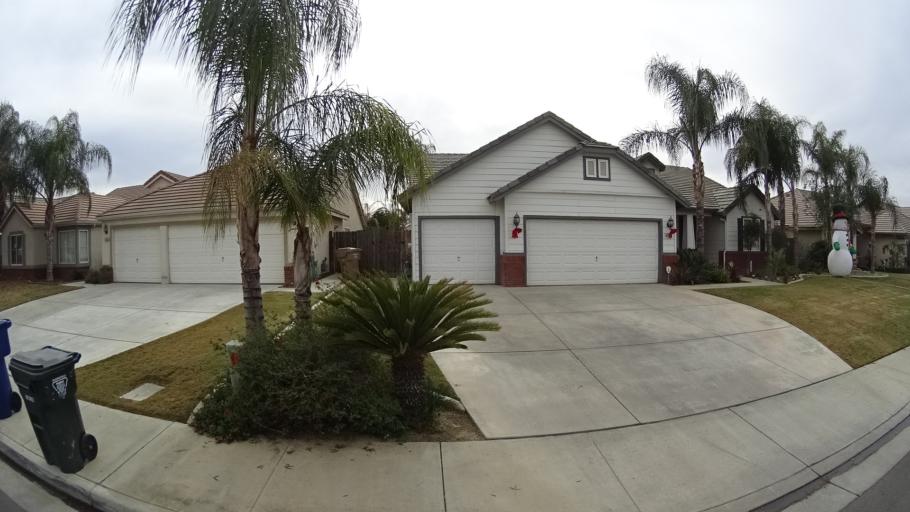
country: US
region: California
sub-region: Kern County
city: Rosedale
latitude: 35.4203
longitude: -119.1295
